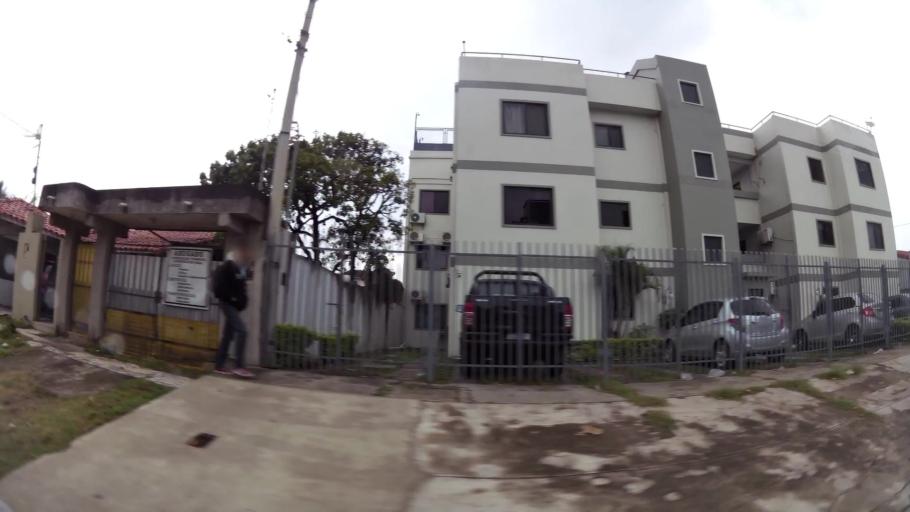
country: BO
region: Santa Cruz
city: Santa Cruz de la Sierra
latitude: -17.7795
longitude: -63.1431
